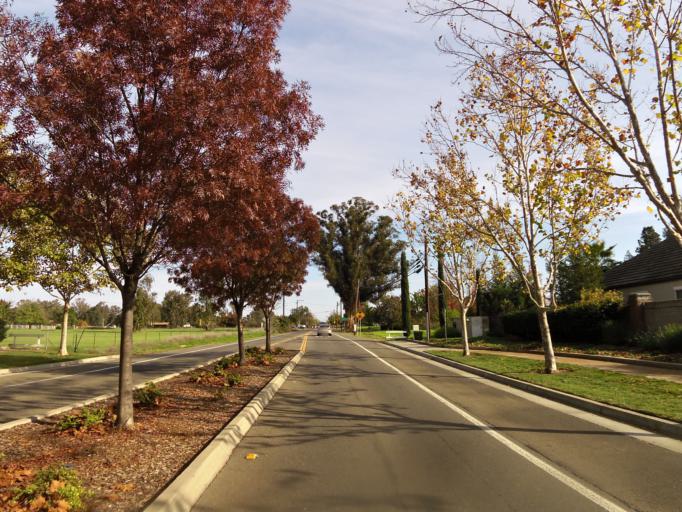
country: US
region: California
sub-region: Sacramento County
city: Elk Grove
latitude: 38.4091
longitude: -121.3371
